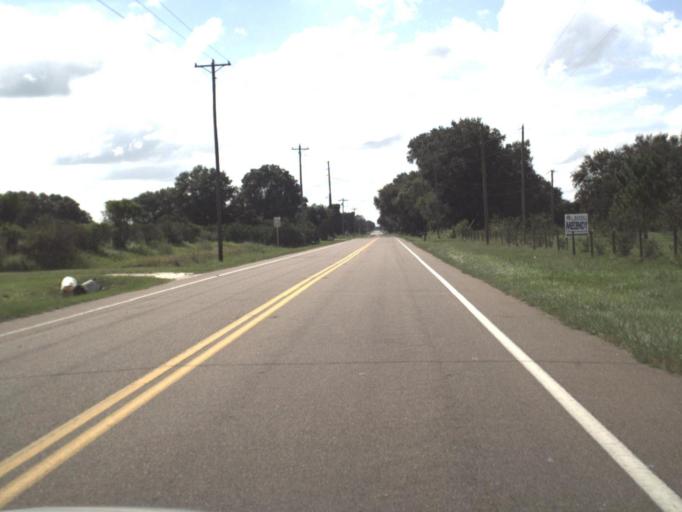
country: US
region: Florida
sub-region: Hardee County
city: Zolfo Springs
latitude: 27.4823
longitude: -81.8734
